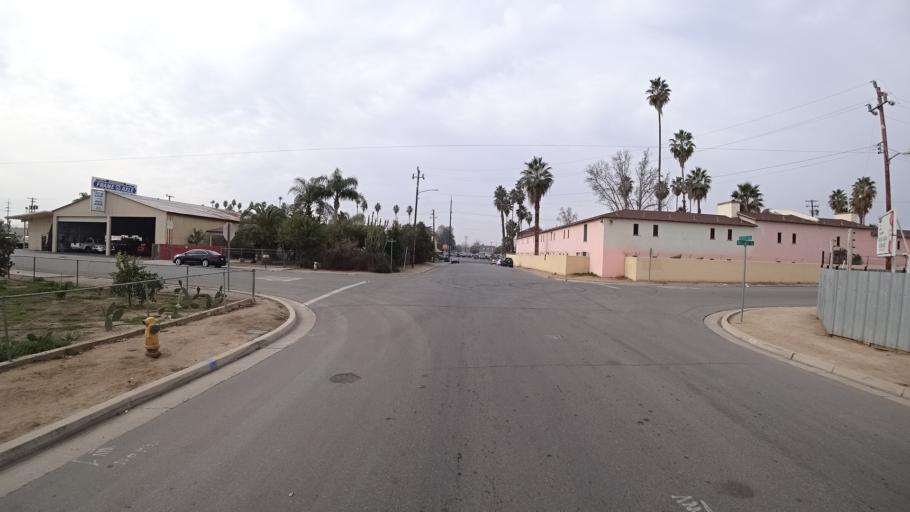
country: US
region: California
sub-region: Kern County
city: Bakersfield
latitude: 35.3674
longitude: -119.0016
